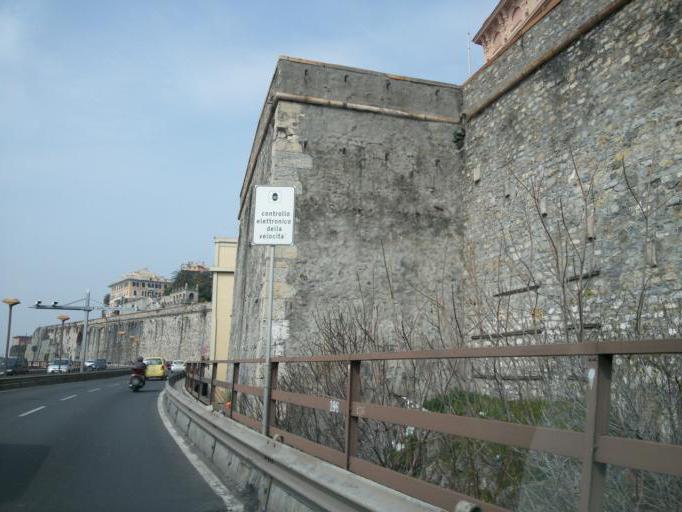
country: IT
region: Liguria
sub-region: Provincia di Genova
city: San Teodoro
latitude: 44.3970
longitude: 8.9405
